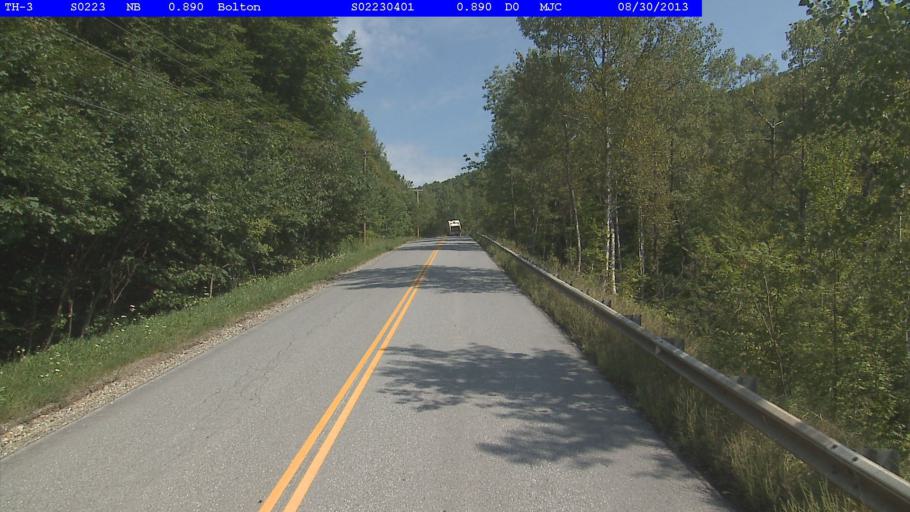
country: US
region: Vermont
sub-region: Washington County
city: Waterbury
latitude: 44.3834
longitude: -72.8742
